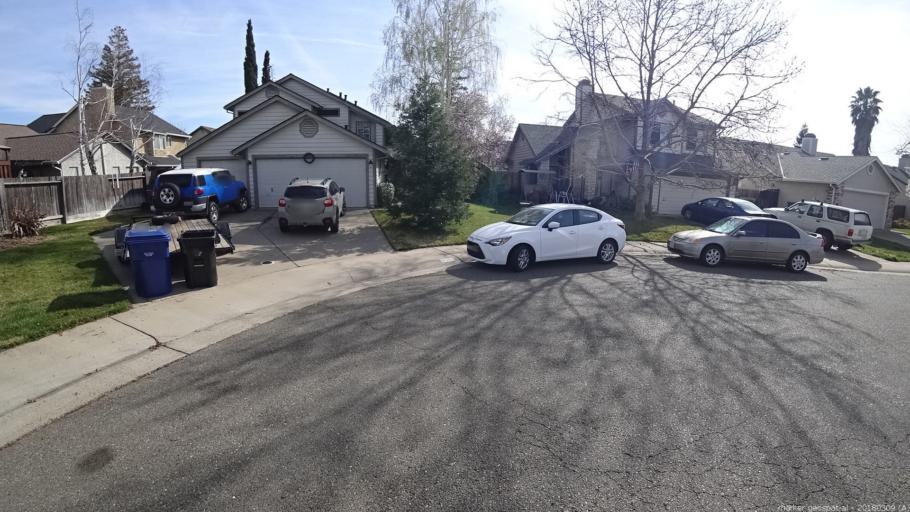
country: US
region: California
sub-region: Sacramento County
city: Florin
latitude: 38.4575
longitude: -121.4000
